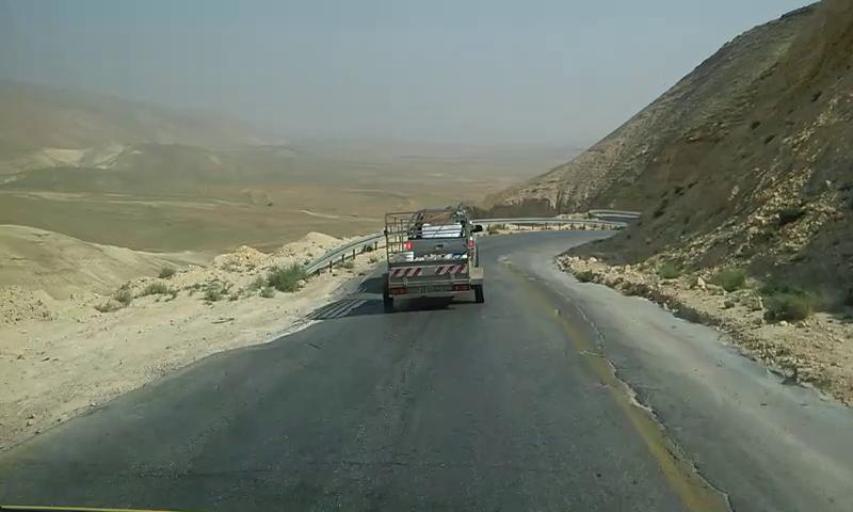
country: PS
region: West Bank
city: An Nuway`imah
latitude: 31.9141
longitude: 35.3847
